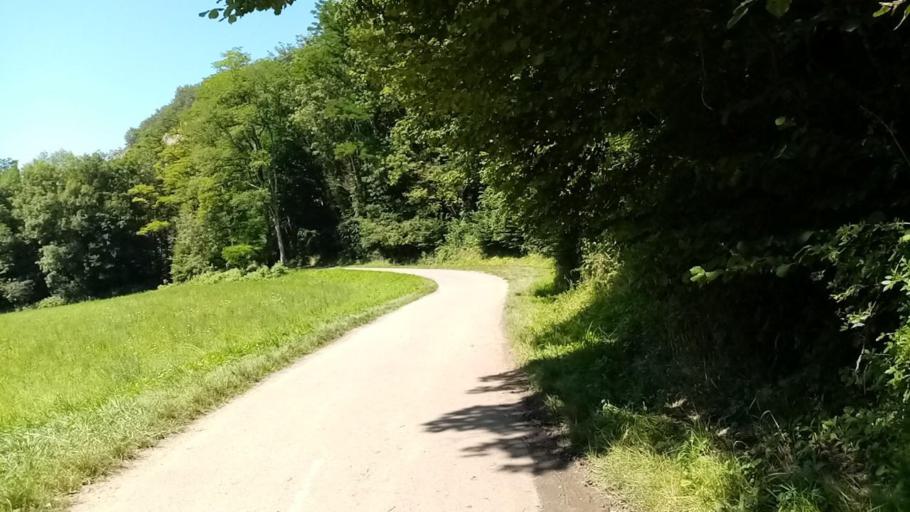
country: FR
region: Bourgogne
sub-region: Departement de la Cote-d'Or
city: Nolay
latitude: 46.9857
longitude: 4.6484
